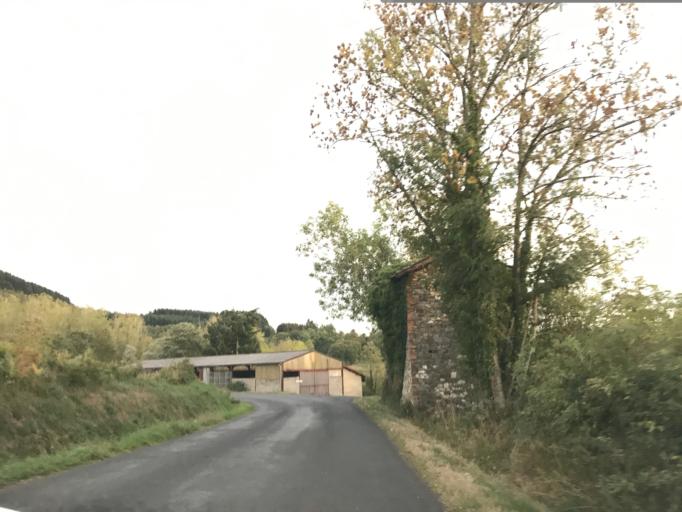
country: FR
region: Auvergne
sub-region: Departement du Puy-de-Dome
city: Escoutoux
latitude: 45.8354
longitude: 3.5480
